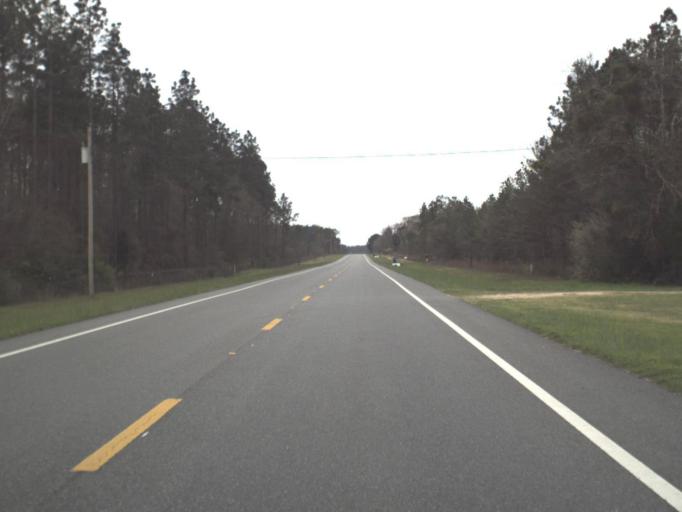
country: US
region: Florida
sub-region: Calhoun County
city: Blountstown
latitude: 30.3938
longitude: -85.2133
